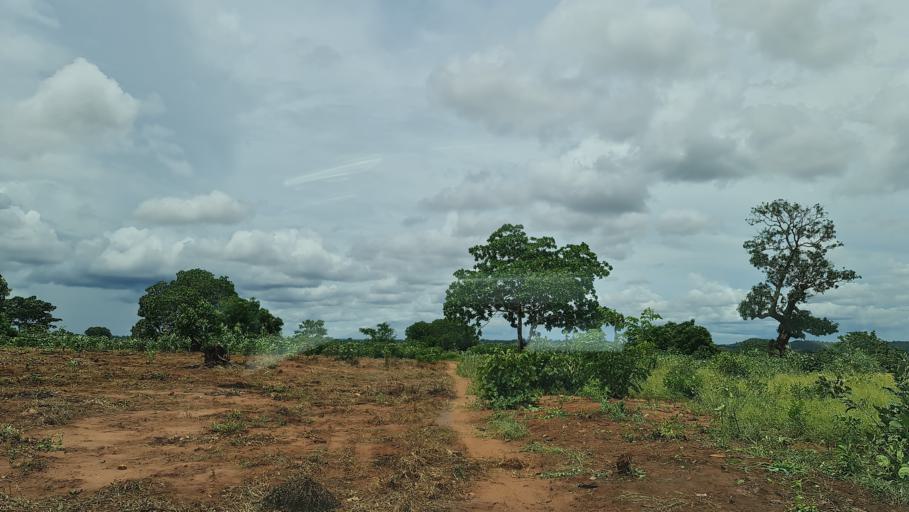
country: MZ
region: Nampula
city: Nacala
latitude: -14.7861
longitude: 39.9799
